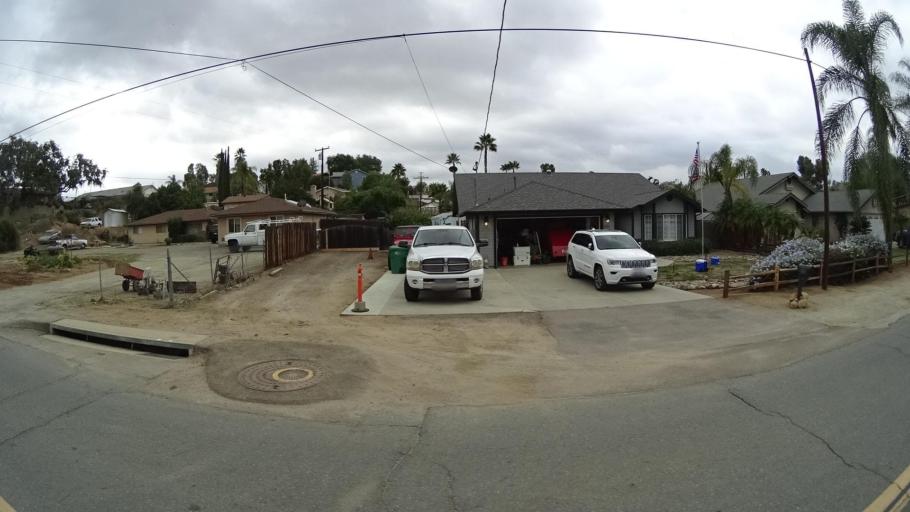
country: US
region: California
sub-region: San Diego County
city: Lakeside
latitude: 32.8594
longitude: -116.9061
